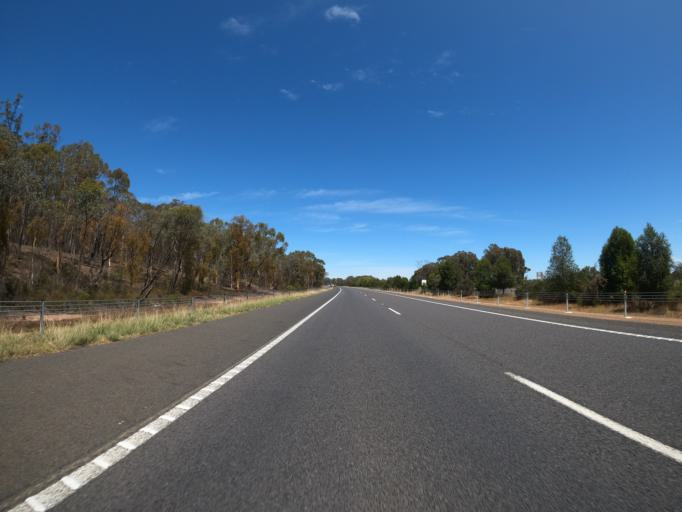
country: AU
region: Victoria
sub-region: Benalla
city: Benalla
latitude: -36.5762
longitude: 145.9283
